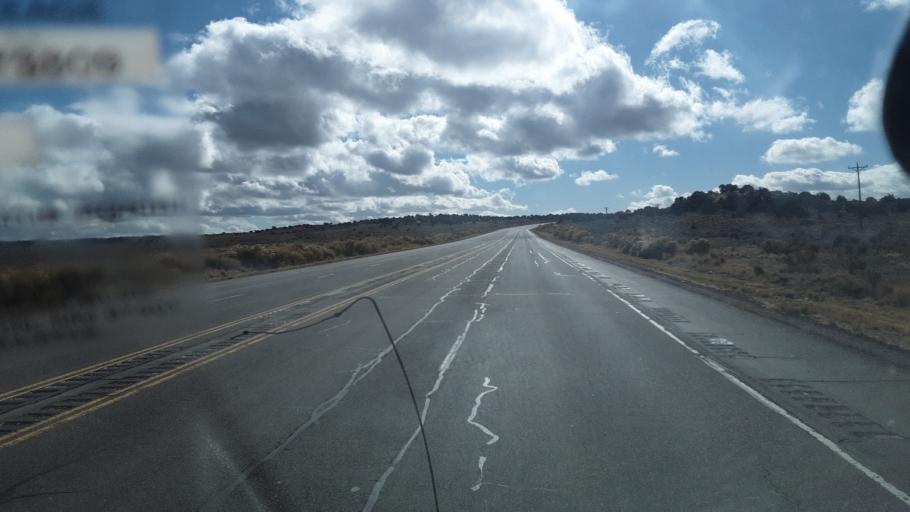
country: US
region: New Mexico
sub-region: San Juan County
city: Bloomfield
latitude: 36.2840
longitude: -107.7486
